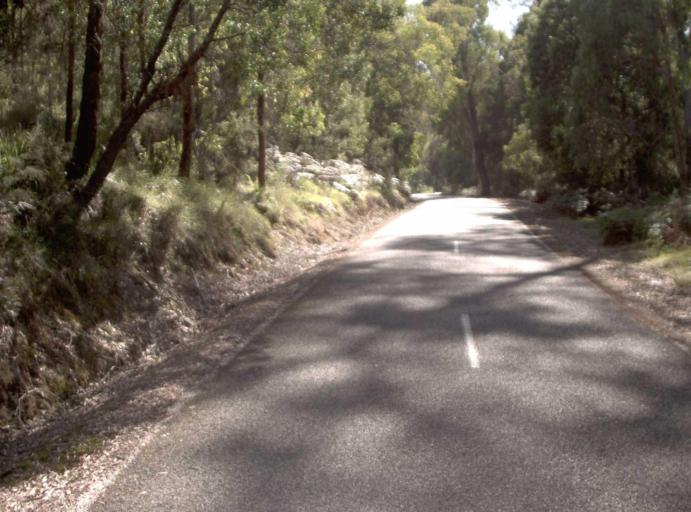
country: AU
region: New South Wales
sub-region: Bombala
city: Bombala
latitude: -37.3788
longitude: 148.6767
